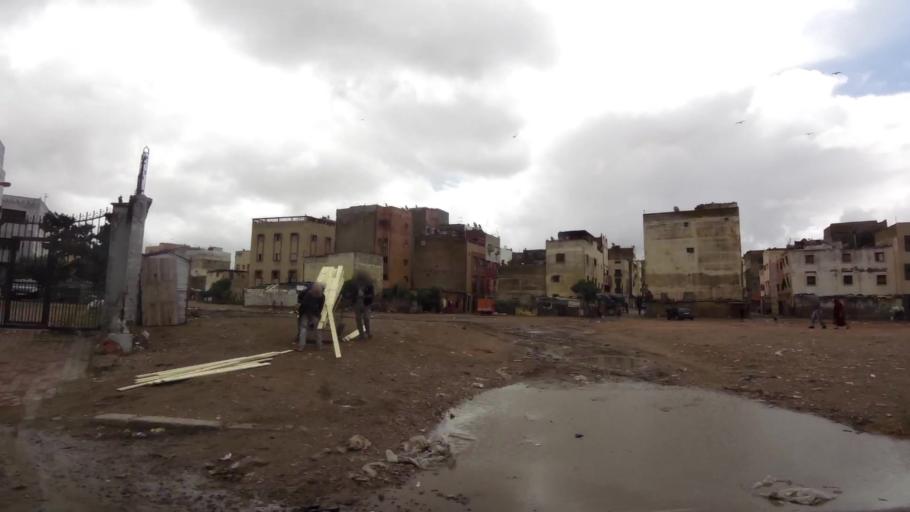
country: MA
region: Grand Casablanca
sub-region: Casablanca
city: Casablanca
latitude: 33.5692
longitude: -7.6892
